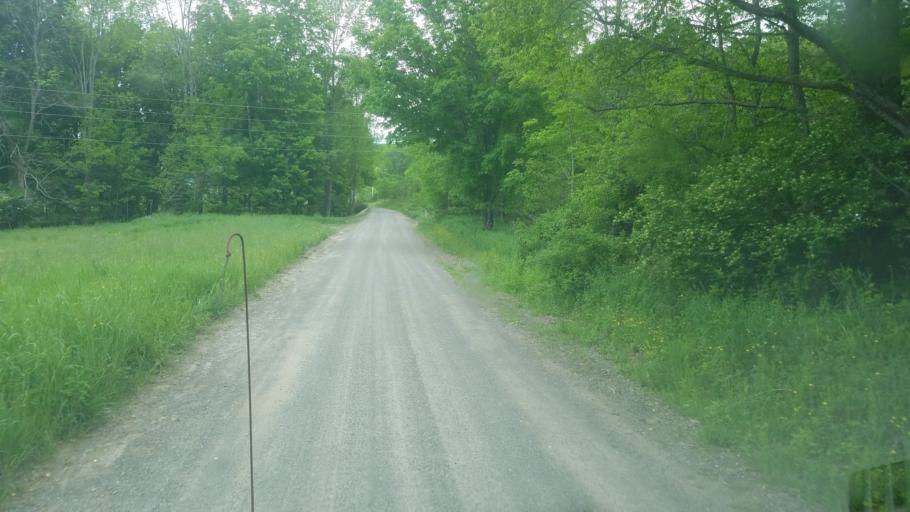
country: US
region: Pennsylvania
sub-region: Tioga County
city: Westfield
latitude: 41.8685
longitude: -77.5973
